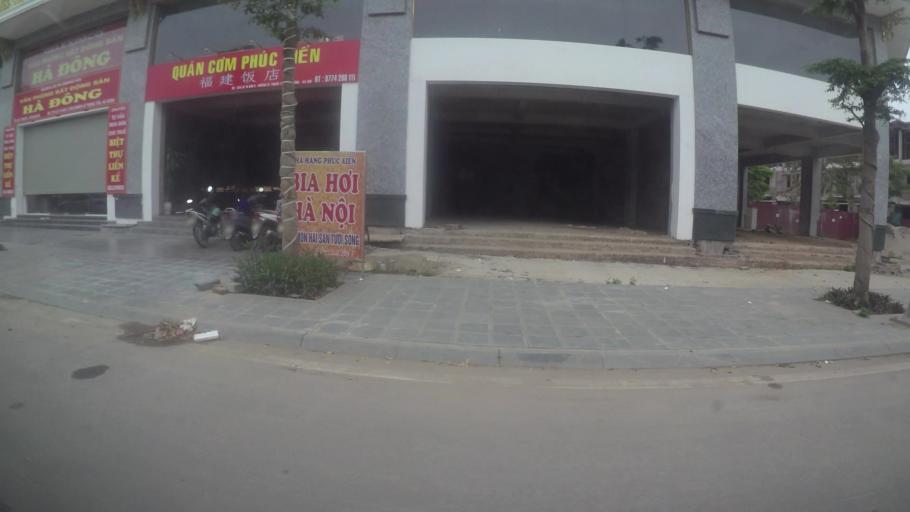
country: VN
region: Ha Noi
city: Ha Dong
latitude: 20.9847
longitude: 105.7404
